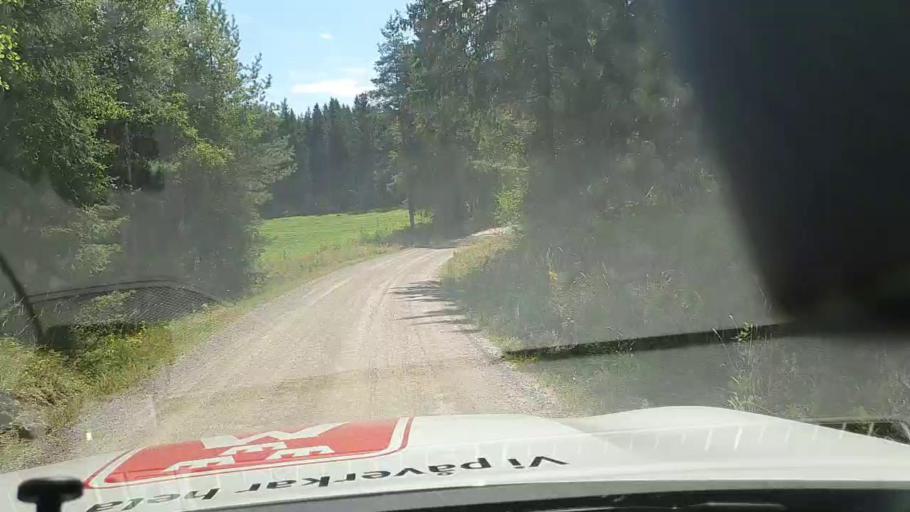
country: SE
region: Soedermanland
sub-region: Strangnas Kommun
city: Akers Styckebruk
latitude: 59.2012
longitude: 16.9189
